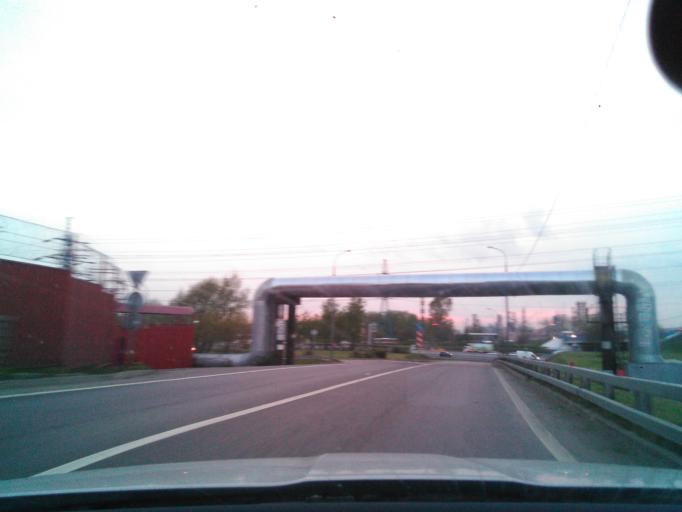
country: RU
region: Moskovskaya
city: Kotel'niki
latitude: 55.6393
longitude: 37.8216
